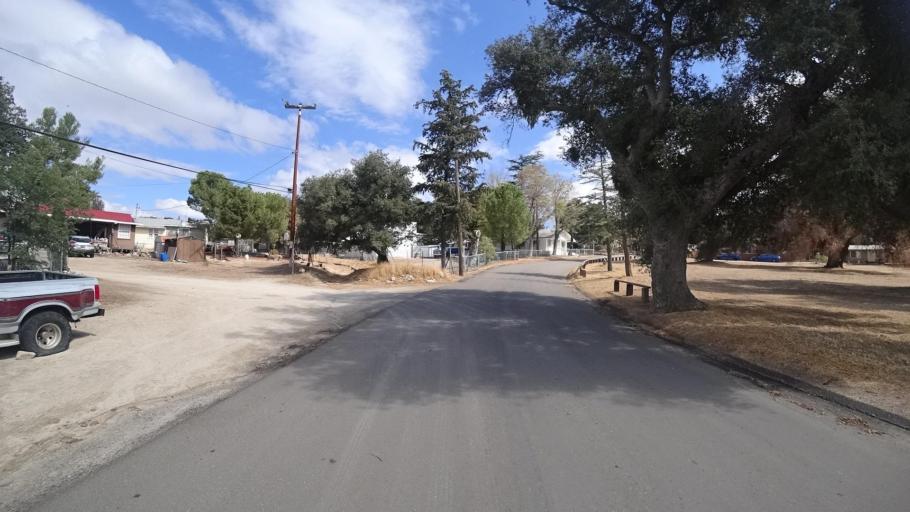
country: US
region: California
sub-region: San Diego County
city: Campo
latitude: 32.6903
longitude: -116.3350
